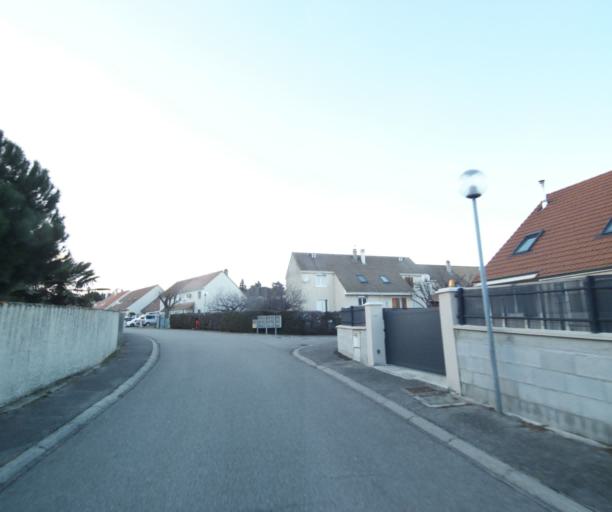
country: FR
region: Rhone-Alpes
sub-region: Departement de l'Ardeche
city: Davezieux
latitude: 45.2539
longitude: 4.7148
